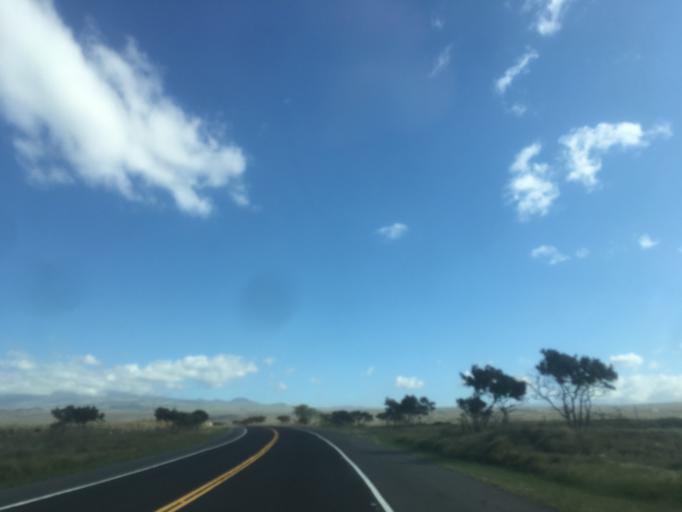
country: US
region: Hawaii
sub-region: Hawaii County
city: Waikoloa
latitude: 19.9083
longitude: -155.7715
